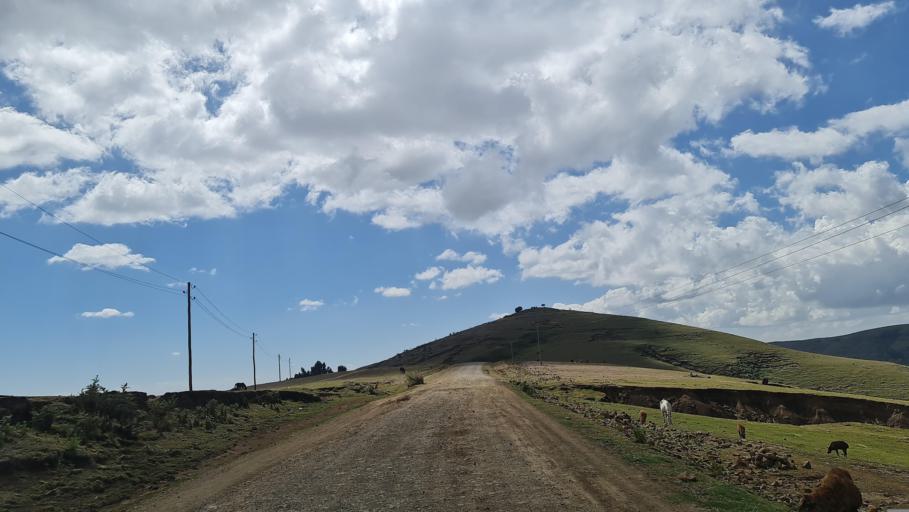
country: ET
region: Amhara
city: Debark'
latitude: 13.1960
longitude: 37.9747
